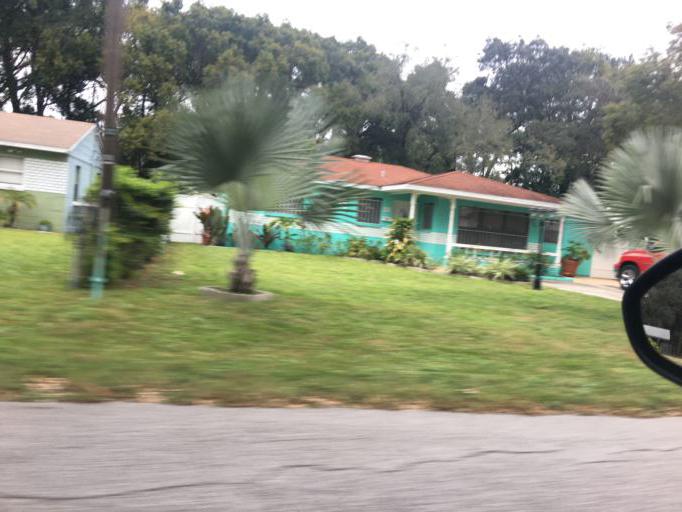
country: US
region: Florida
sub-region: Hillsborough County
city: Carrollwood
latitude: 28.0368
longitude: -82.4649
